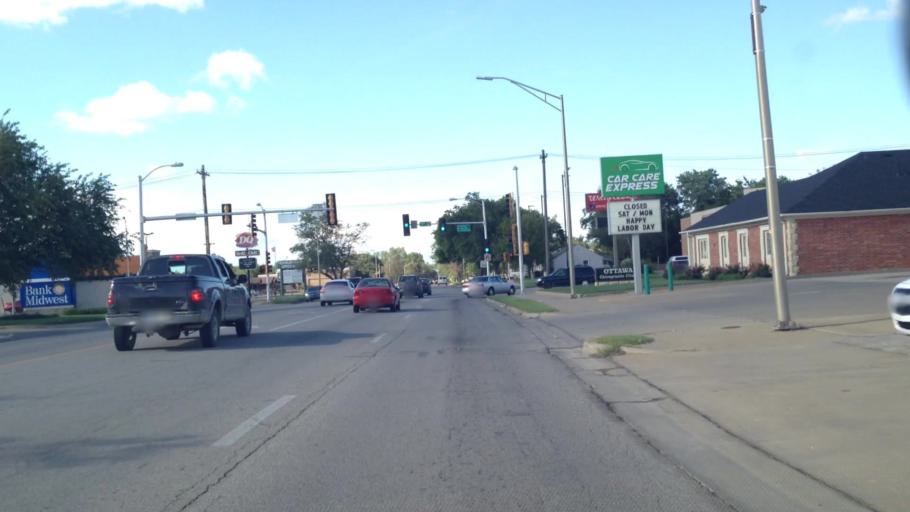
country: US
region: Kansas
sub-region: Franklin County
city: Ottawa
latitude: 38.5932
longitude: -95.2687
